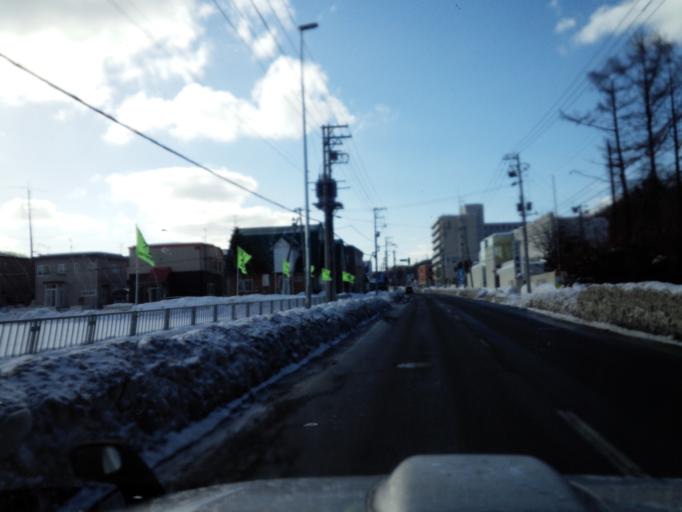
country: JP
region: Hokkaido
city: Sapporo
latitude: 42.9576
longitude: 141.3438
